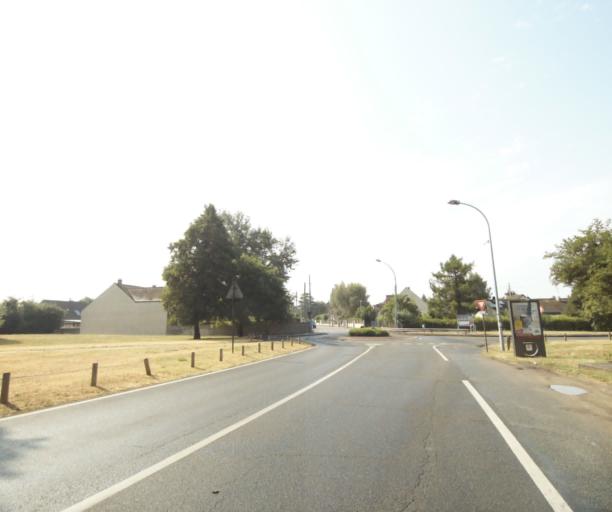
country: FR
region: Ile-de-France
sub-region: Departement des Yvelines
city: Maurecourt
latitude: 49.0022
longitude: 2.0754
